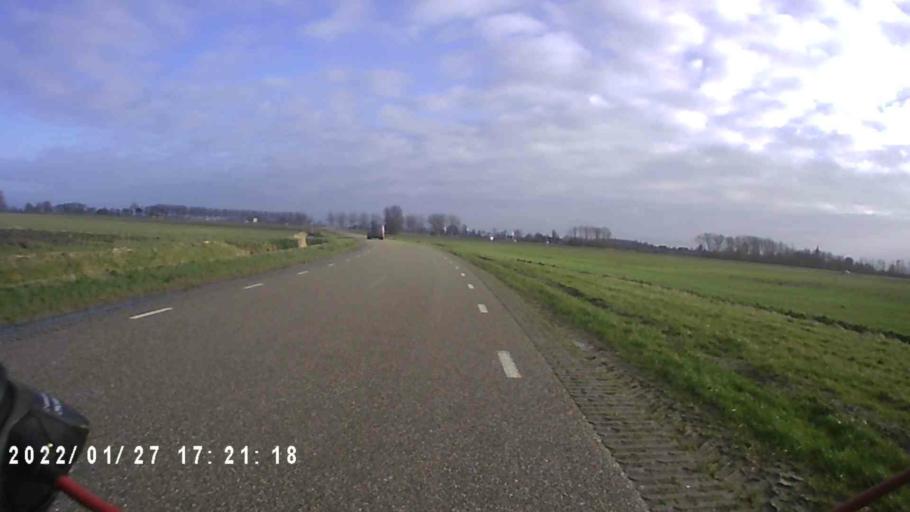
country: NL
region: Friesland
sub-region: Gemeente Dongeradeel
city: Anjum
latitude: 53.3823
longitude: 6.1198
